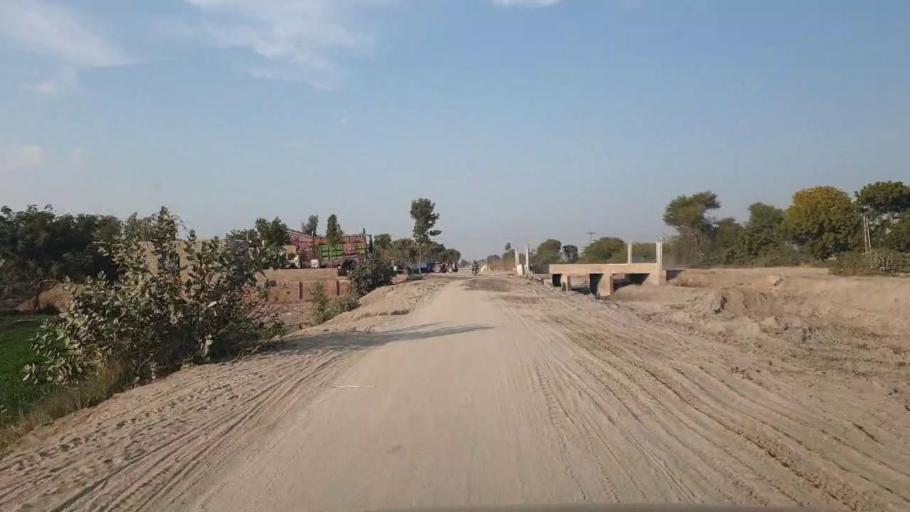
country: PK
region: Sindh
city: Shahpur Chakar
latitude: 26.1571
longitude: 68.6407
